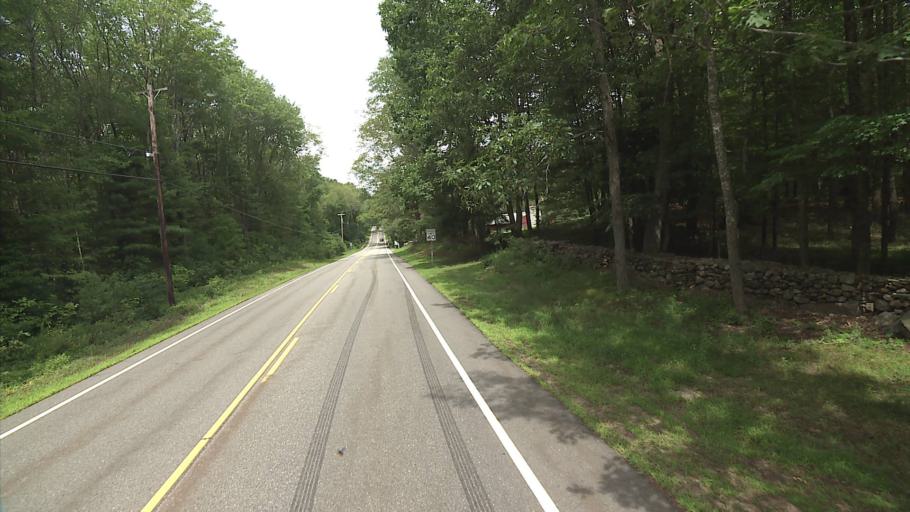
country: US
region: Massachusetts
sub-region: Hampden County
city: Holland
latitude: 41.9509
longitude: -72.1055
